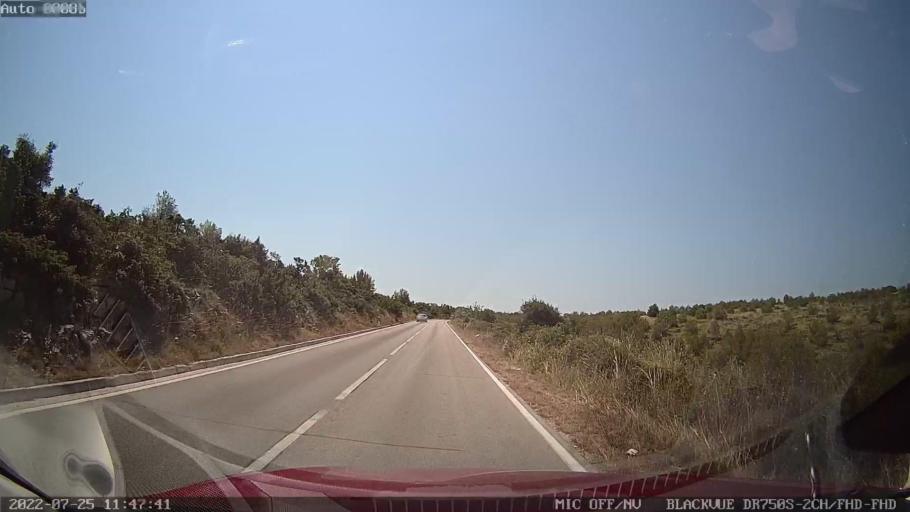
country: HR
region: Zadarska
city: Razanac
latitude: 44.2363
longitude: 15.3024
